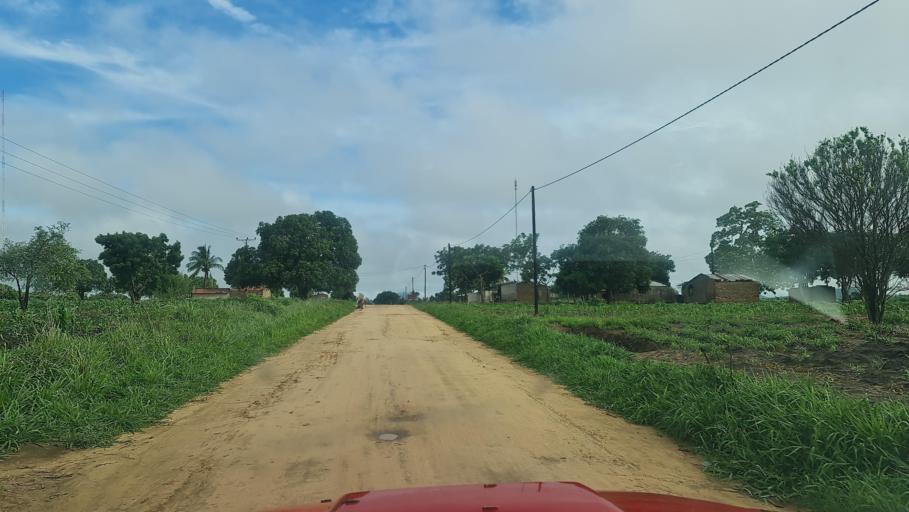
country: MW
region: Southern Region
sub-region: Nsanje District
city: Nsanje
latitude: -17.2999
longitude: 35.5937
